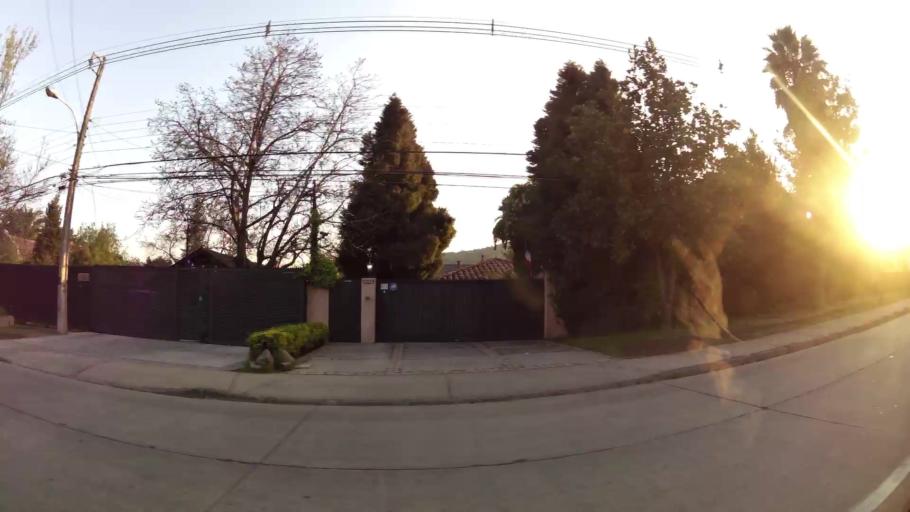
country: CL
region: Santiago Metropolitan
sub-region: Provincia de Santiago
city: Villa Presidente Frei, Nunoa, Santiago, Chile
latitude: -33.3410
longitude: -70.5239
